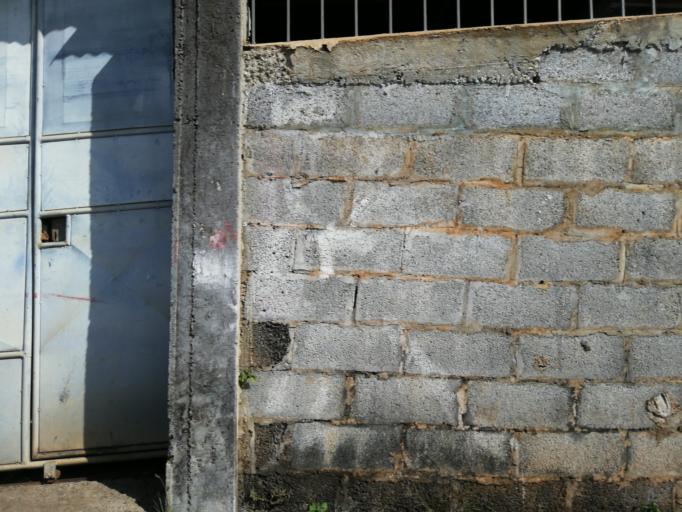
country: MU
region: Black River
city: Petite Riviere
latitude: -20.2211
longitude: 57.4575
